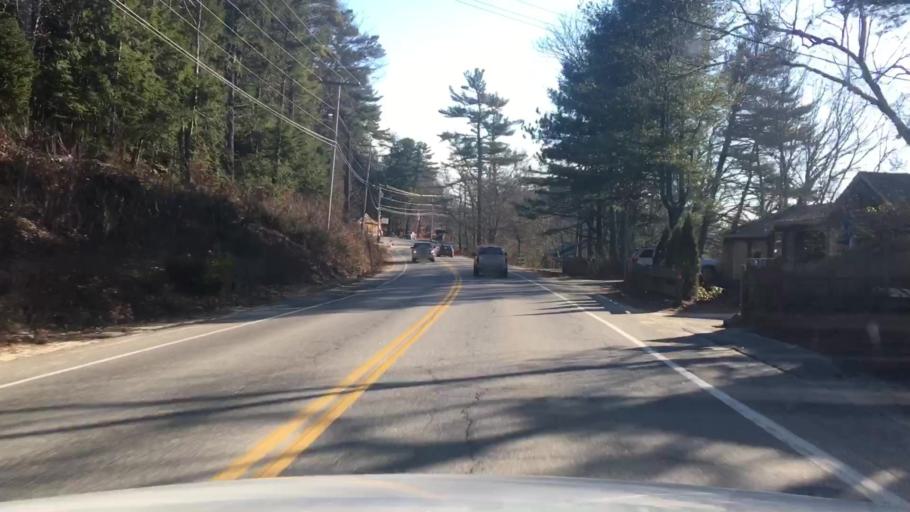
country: US
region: Maine
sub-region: Cumberland County
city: Brunswick
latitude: 43.8641
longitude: -69.9138
